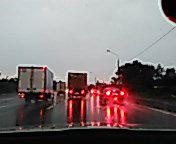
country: RU
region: Moskovskaya
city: Novopodrezkovo
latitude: 55.9341
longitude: 37.3740
